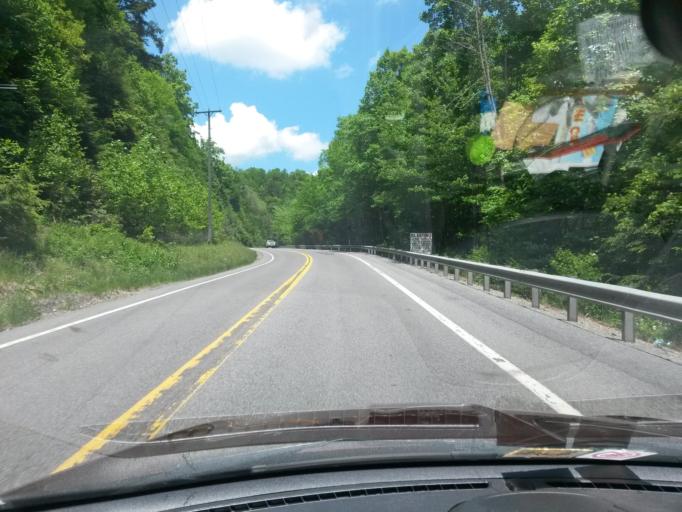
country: US
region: West Virginia
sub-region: Wyoming County
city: Pineville
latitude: 37.6001
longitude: -81.4916
